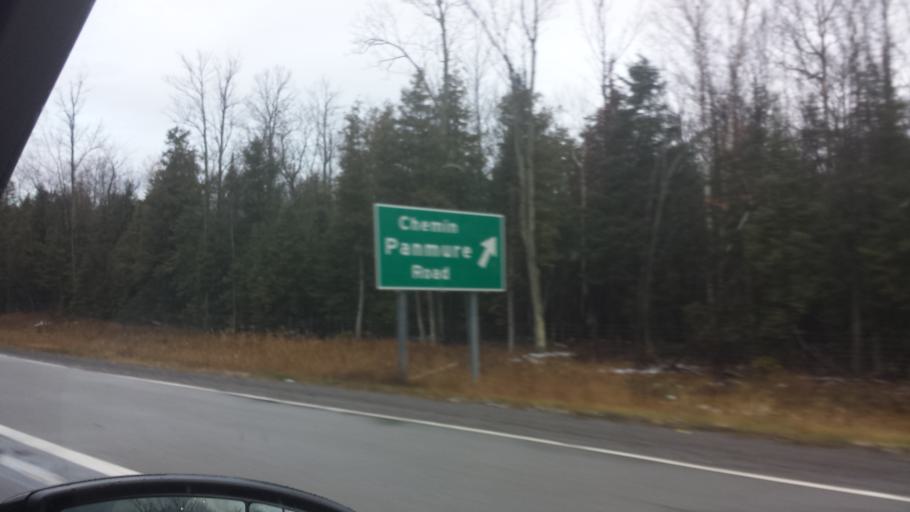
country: CA
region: Ontario
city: Carleton Place
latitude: 45.3313
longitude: -76.1531
